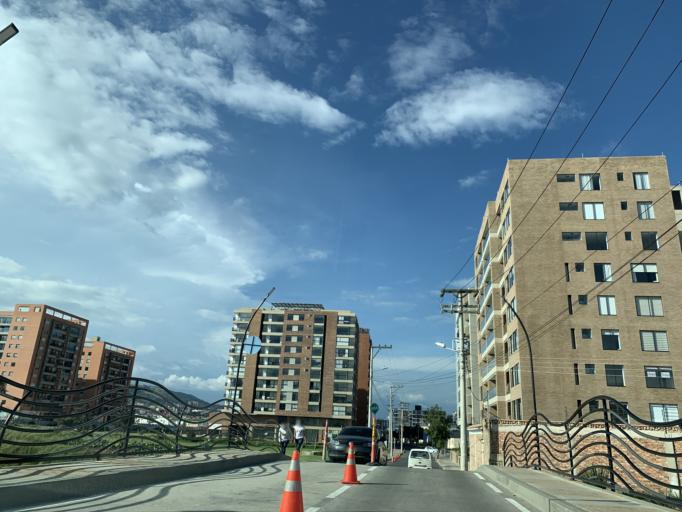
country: CO
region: Boyaca
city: Tunja
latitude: 5.5447
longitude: -73.3514
